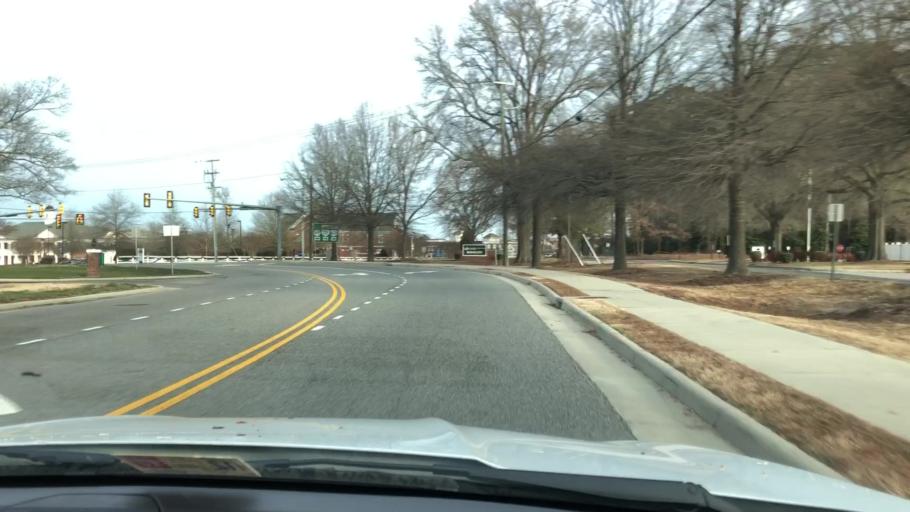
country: US
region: Virginia
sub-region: James City County
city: Williamsburg
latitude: 37.2734
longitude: -76.7388
